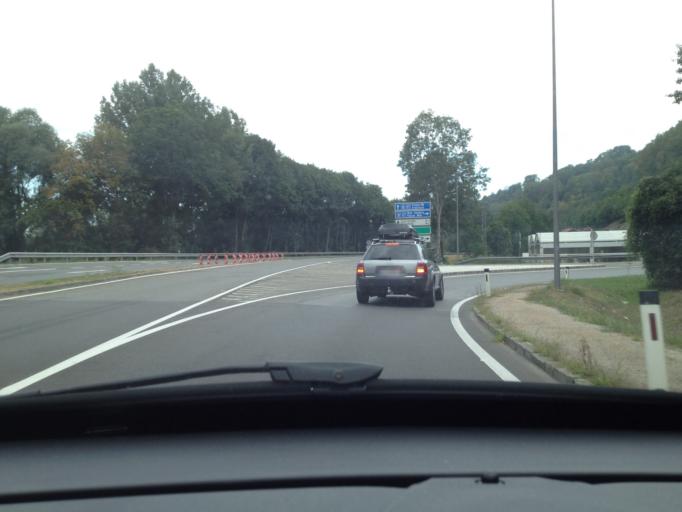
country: AT
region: Upper Austria
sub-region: Politischer Bezirk Urfahr-Umgebung
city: Steyregg
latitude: 48.2895
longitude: 14.3462
